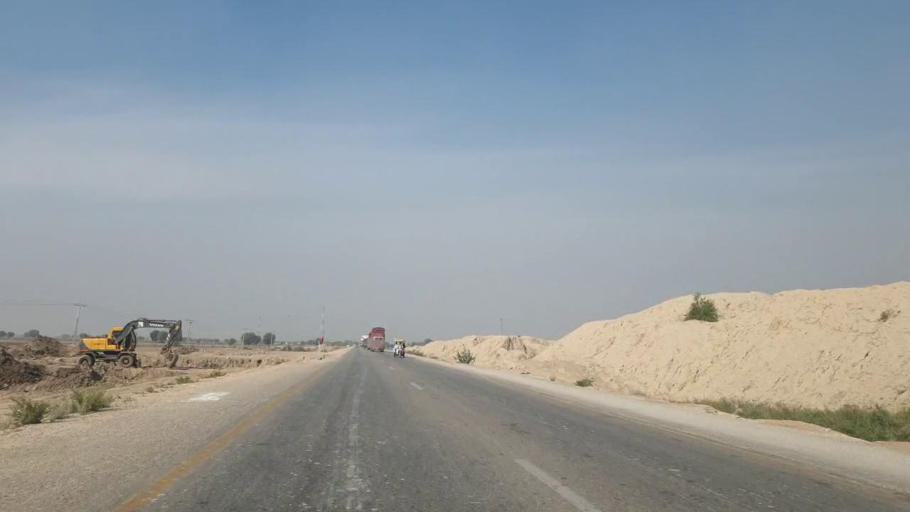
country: PK
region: Sindh
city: Sann
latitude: 25.9738
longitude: 68.1871
